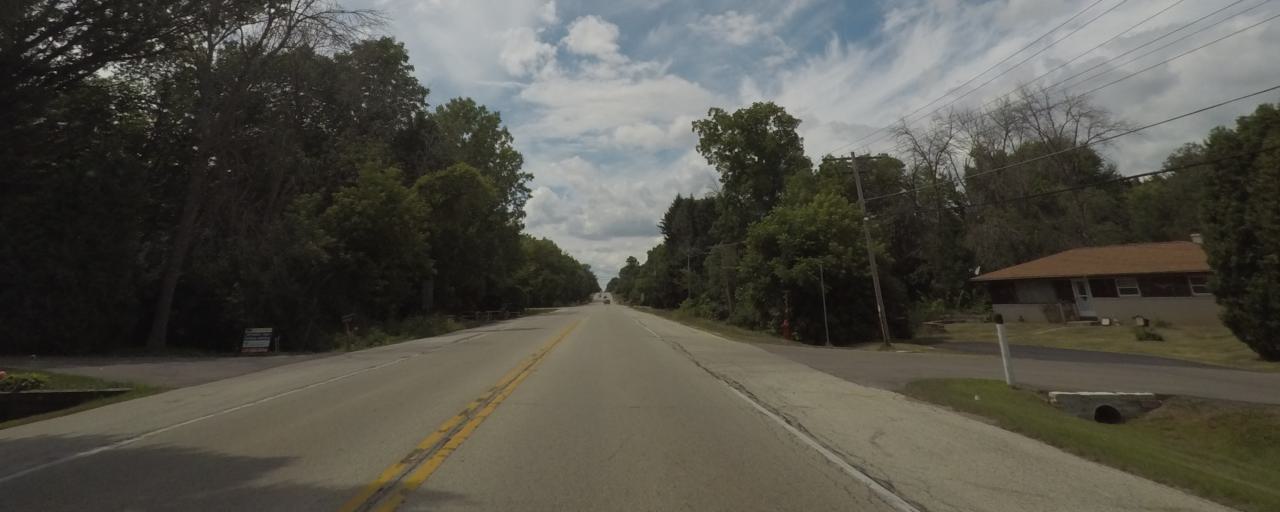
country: US
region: Wisconsin
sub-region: Waukesha County
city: New Berlin
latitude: 42.9956
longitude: -88.0713
